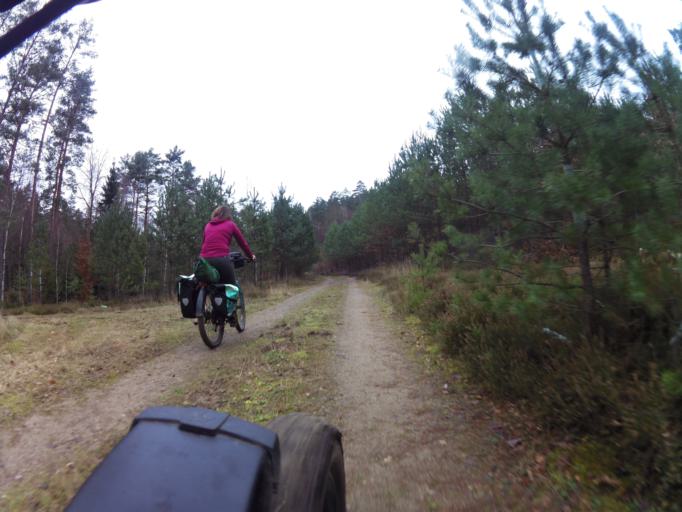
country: PL
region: West Pomeranian Voivodeship
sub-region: Powiat koszalinski
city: Polanow
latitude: 54.0437
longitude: 16.6589
